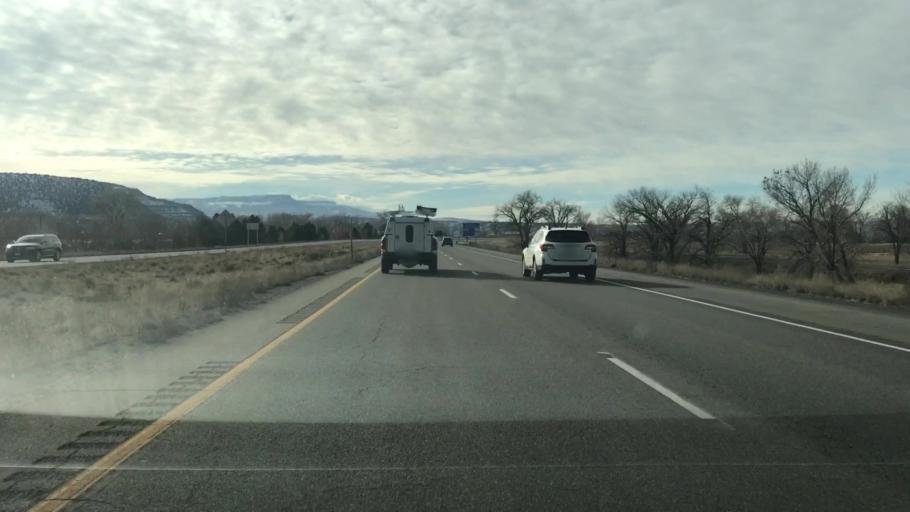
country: US
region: Colorado
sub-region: Garfield County
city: Parachute
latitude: 39.3365
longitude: -108.1941
